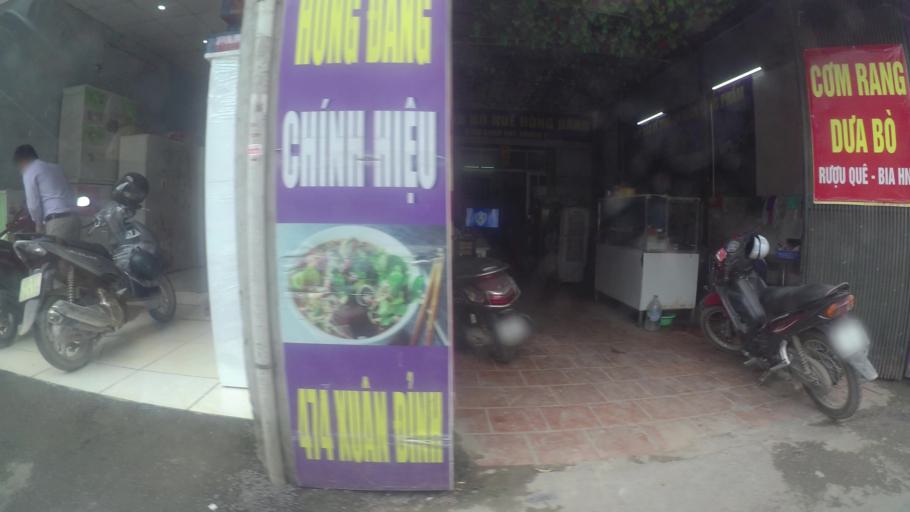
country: VN
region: Ha Noi
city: Tay Ho
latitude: 21.0744
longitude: 105.7886
